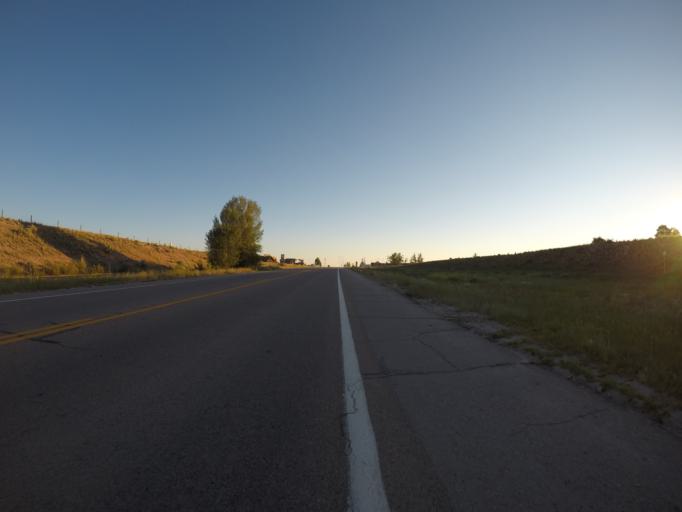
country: US
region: Wyoming
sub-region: Sublette County
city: Marbleton
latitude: 42.5498
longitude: -110.1096
